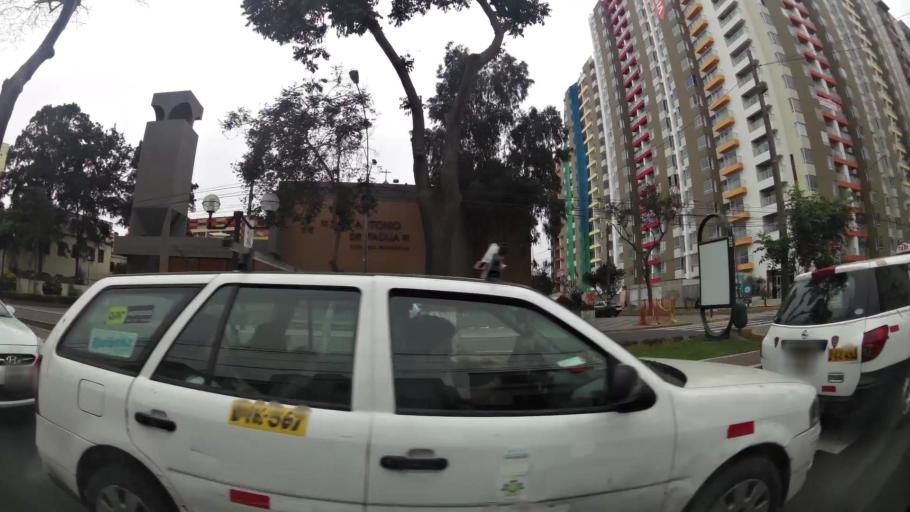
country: PE
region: Lima
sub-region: Lima
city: San Isidro
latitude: -12.0833
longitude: -77.0524
